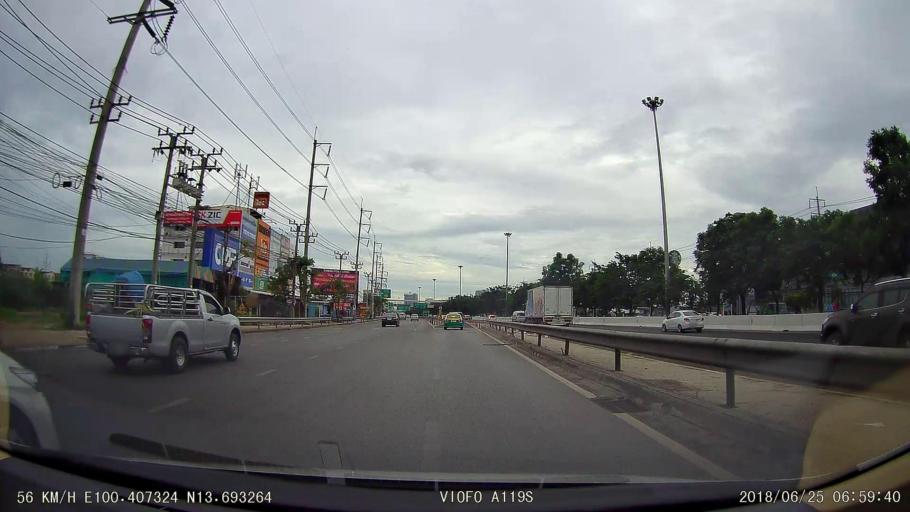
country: TH
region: Bangkok
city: Bang Khae
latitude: 13.6934
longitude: 100.4073
